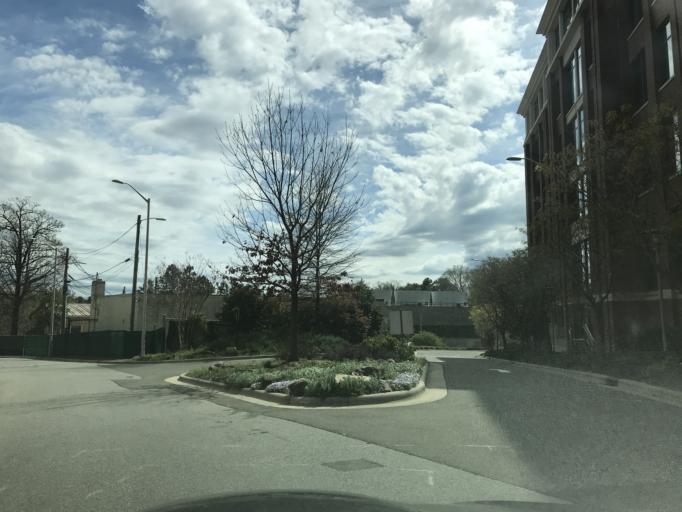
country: US
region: North Carolina
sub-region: Orange County
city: Chapel Hill
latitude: 35.9015
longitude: -79.0537
